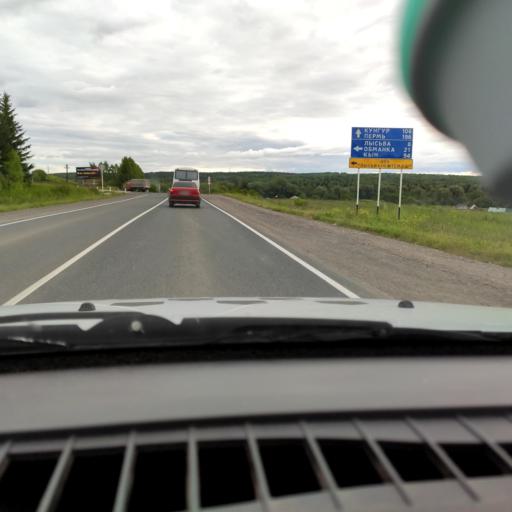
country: RU
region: Perm
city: Lys'va
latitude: 58.1644
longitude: 57.7774
